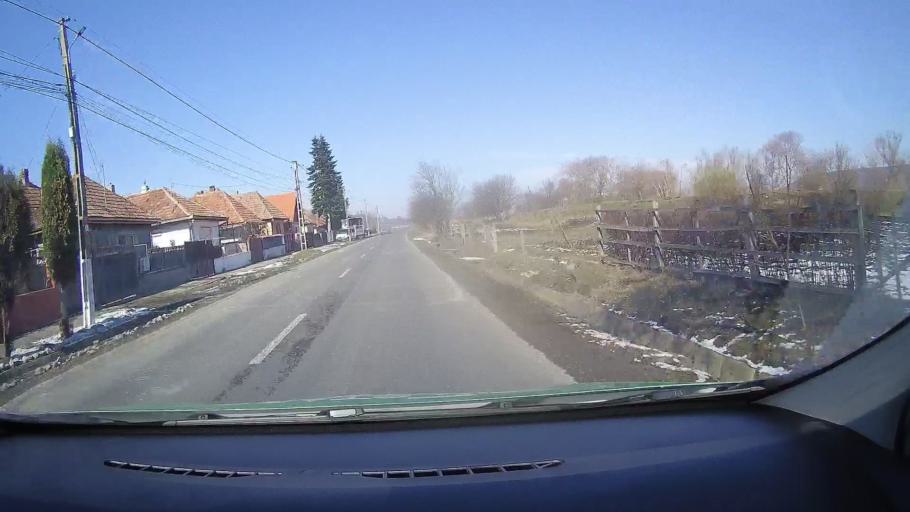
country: RO
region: Brasov
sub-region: Comuna Homorod
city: Homorod
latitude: 46.0216
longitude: 25.2744
